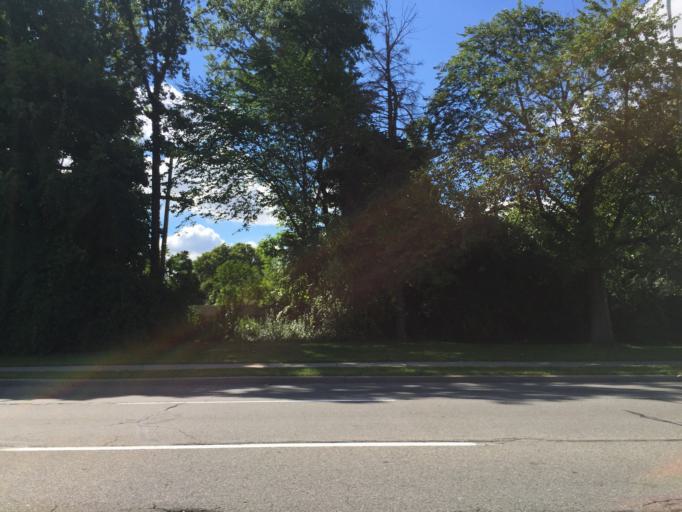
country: US
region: Michigan
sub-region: Oakland County
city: Hazel Park
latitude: 42.4337
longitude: -83.1164
